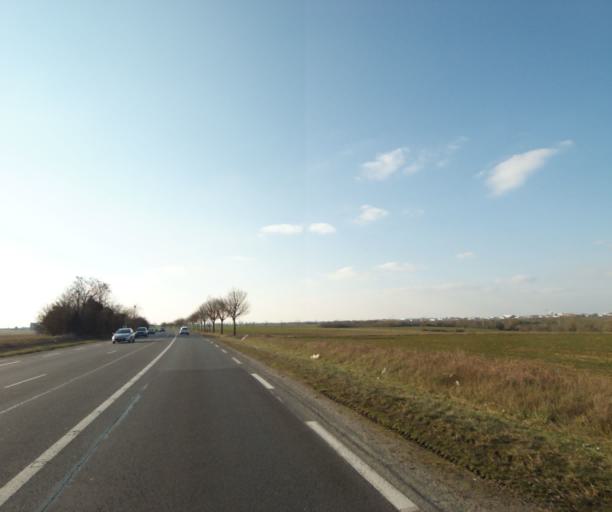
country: FR
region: Poitou-Charentes
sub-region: Departement des Deux-Sevres
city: Vouille
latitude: 46.3174
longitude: -0.3899
